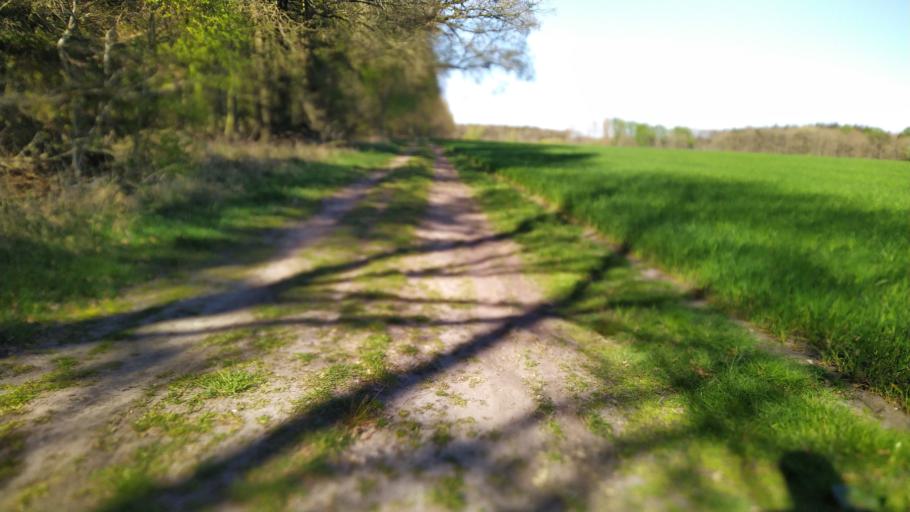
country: DE
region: Lower Saxony
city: Klein Meckelsen
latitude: 53.2955
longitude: 9.4281
